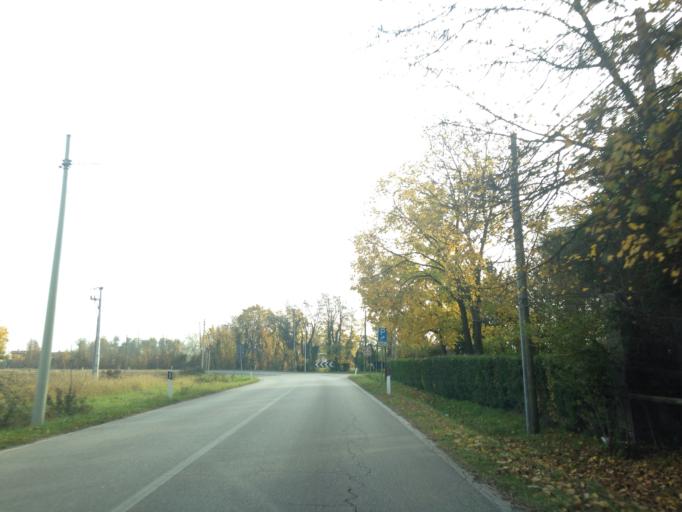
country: IT
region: Friuli Venezia Giulia
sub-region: Provincia di Pordenone
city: Brugnera
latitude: 45.8898
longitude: 12.5304
